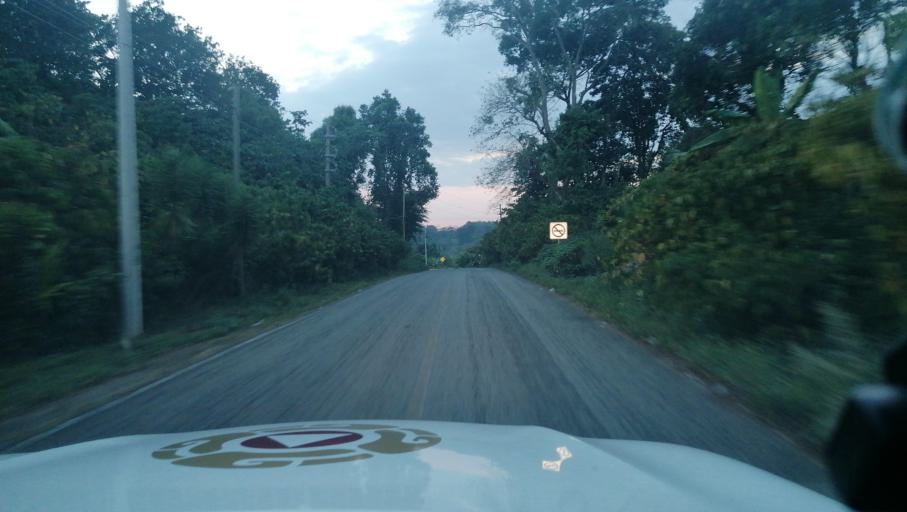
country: MX
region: Chiapas
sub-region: Cacahoatan
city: Benito Juarez
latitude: 15.0293
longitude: -92.2406
